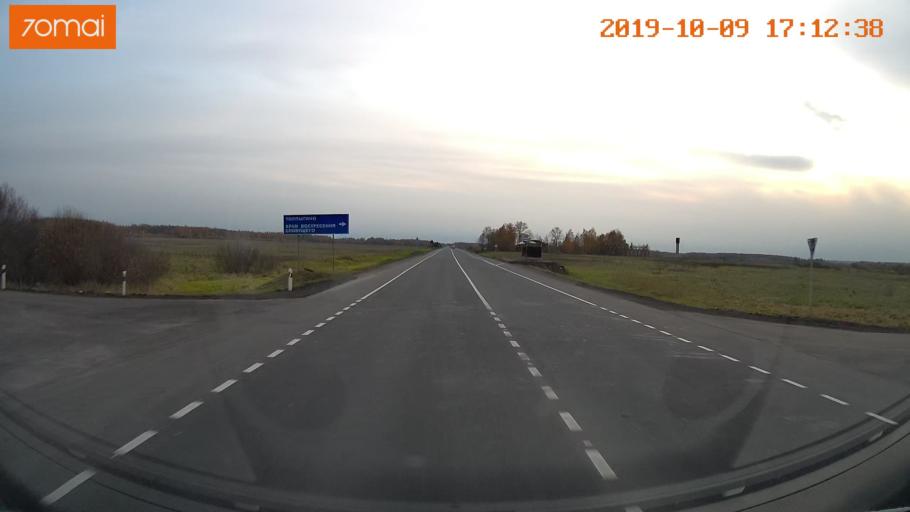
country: RU
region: Ivanovo
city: Privolzhsk
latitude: 57.3262
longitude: 41.2388
